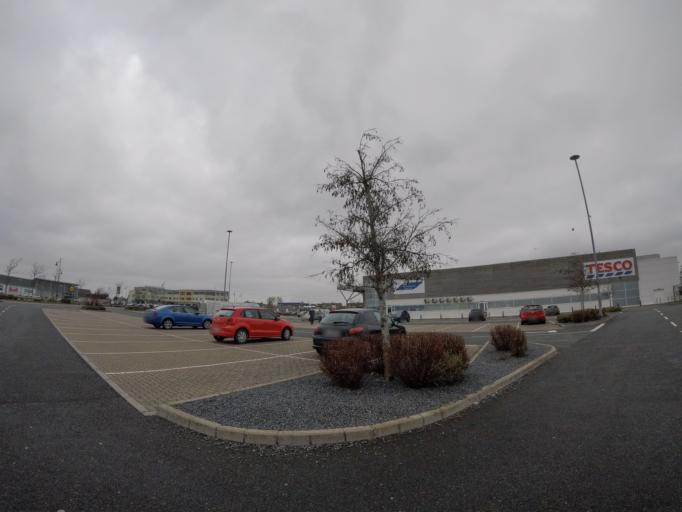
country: IE
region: Munster
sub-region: Waterford
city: Tra Mhor
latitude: 52.1627
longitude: -7.1613
